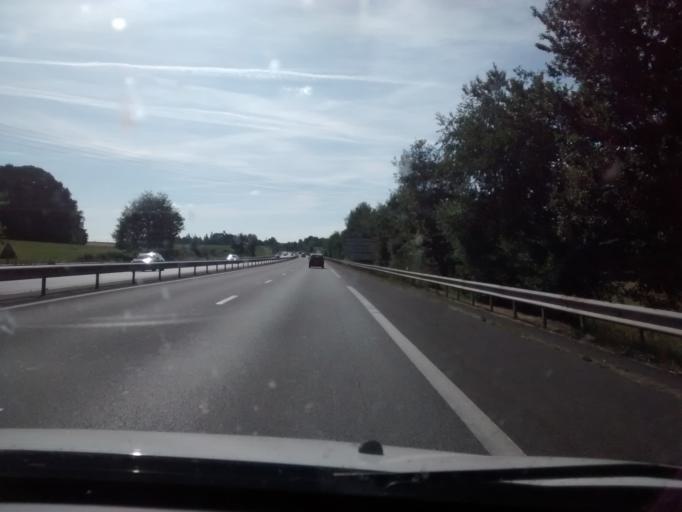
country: FR
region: Brittany
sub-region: Departement d'Ille-et-Vilaine
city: Erbree
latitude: 48.0888
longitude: -1.0748
